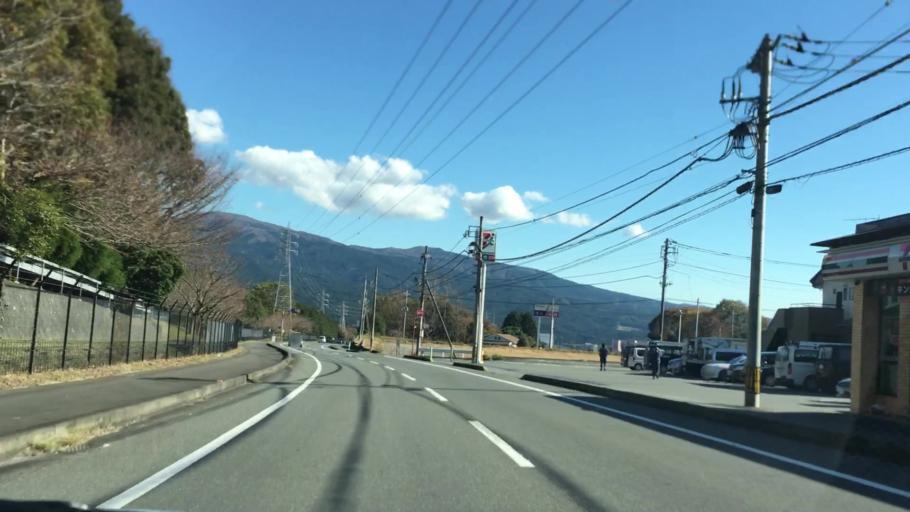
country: JP
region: Shizuoka
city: Gotemba
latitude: 35.2218
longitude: 138.9000
